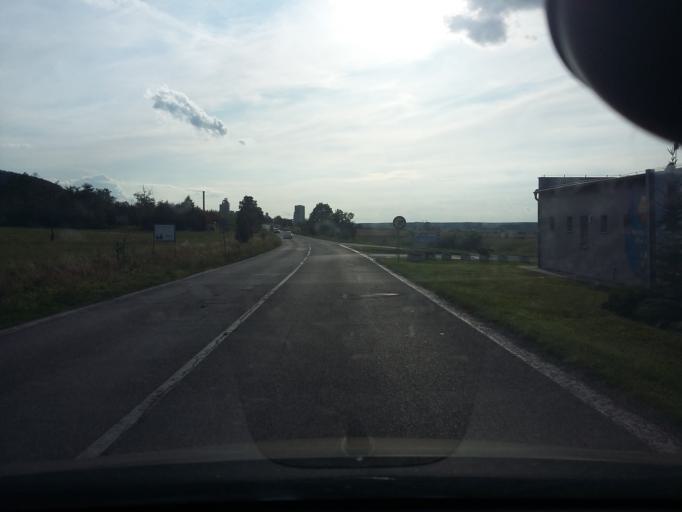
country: SK
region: Bratislavsky
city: Modra
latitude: 48.4636
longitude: 17.2230
